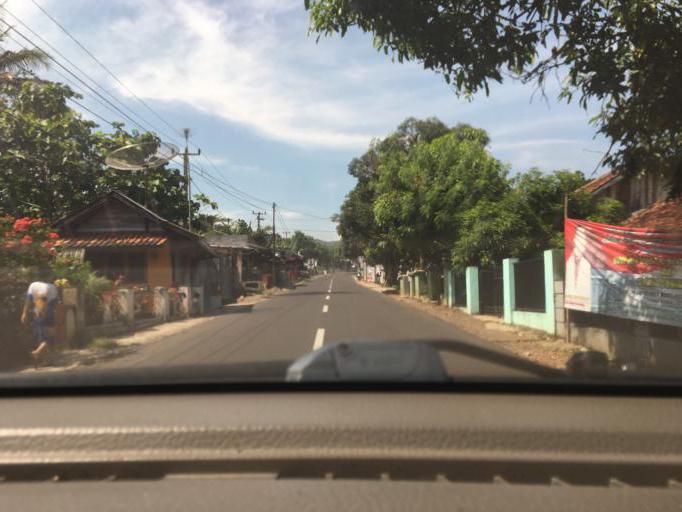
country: ID
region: West Java
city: Cilengkrang
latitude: -6.9500
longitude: 108.0933
